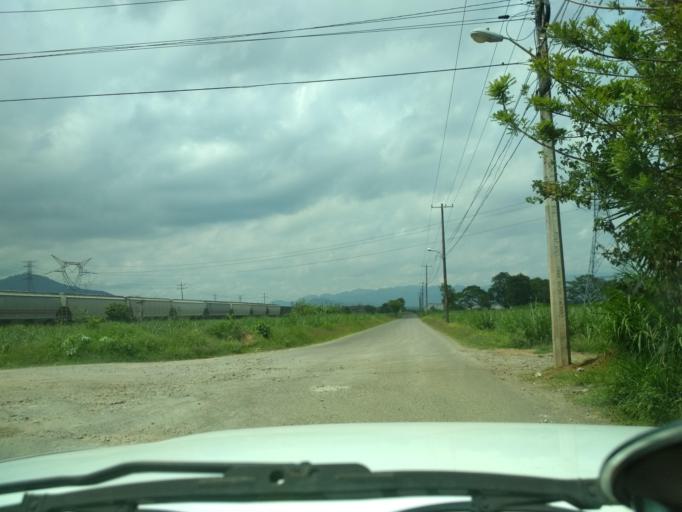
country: MX
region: Veracruz
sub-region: Ixtaczoquitlan
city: Buenavista
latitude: 18.8883
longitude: -97.0463
